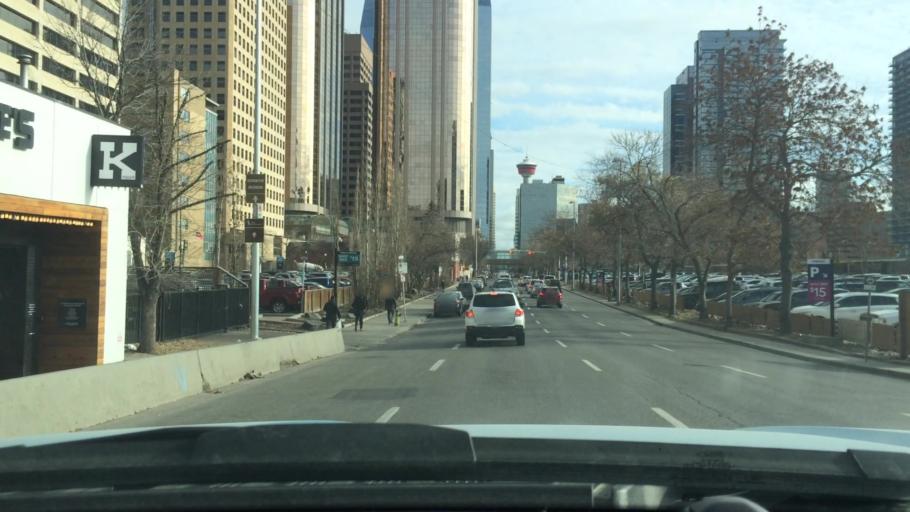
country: CA
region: Alberta
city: Calgary
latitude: 51.0451
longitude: -114.0812
